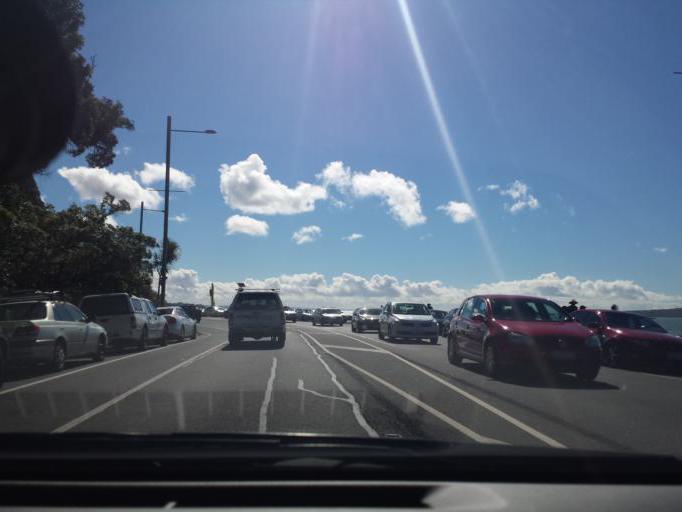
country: NZ
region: Auckland
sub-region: Auckland
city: Tamaki
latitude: -36.8463
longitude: 174.8283
